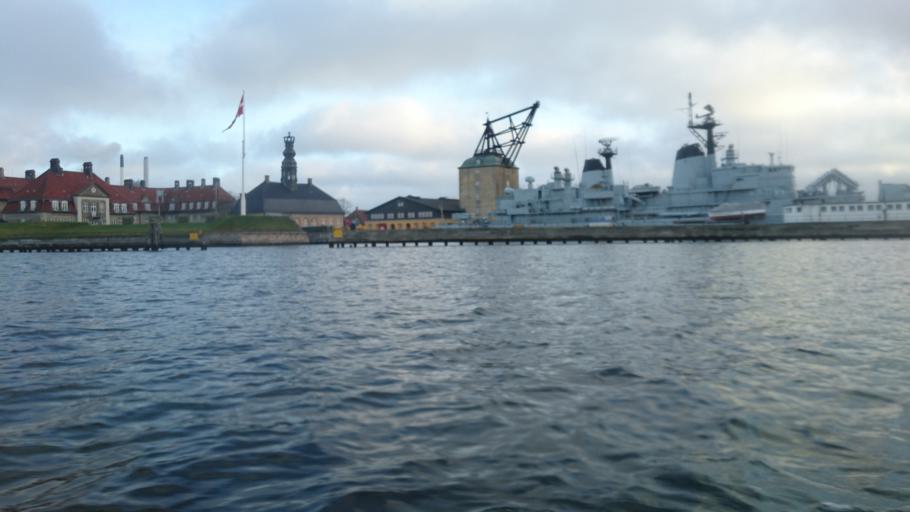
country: DK
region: Capital Region
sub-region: Kobenhavn
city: Christianshavn
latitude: 55.6898
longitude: 12.6043
